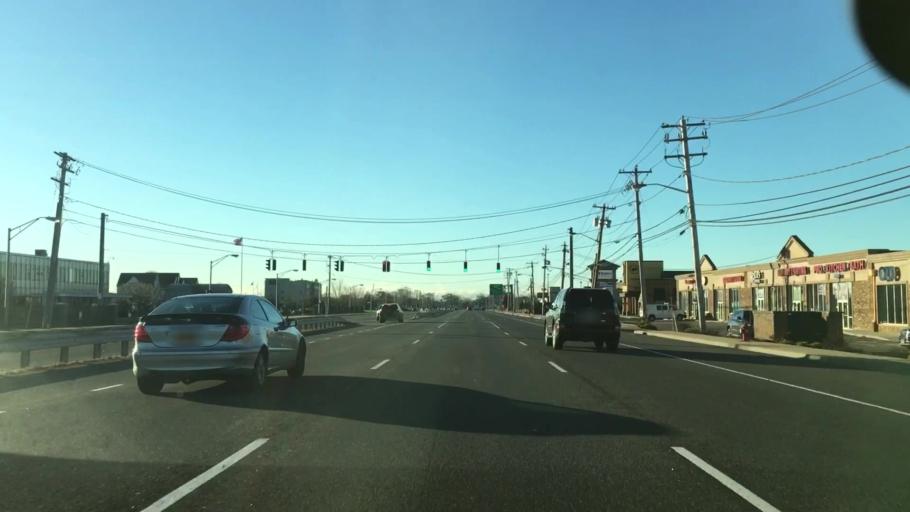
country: US
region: New York
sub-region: Suffolk County
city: East Farmingdale
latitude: 40.7330
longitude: -73.4237
